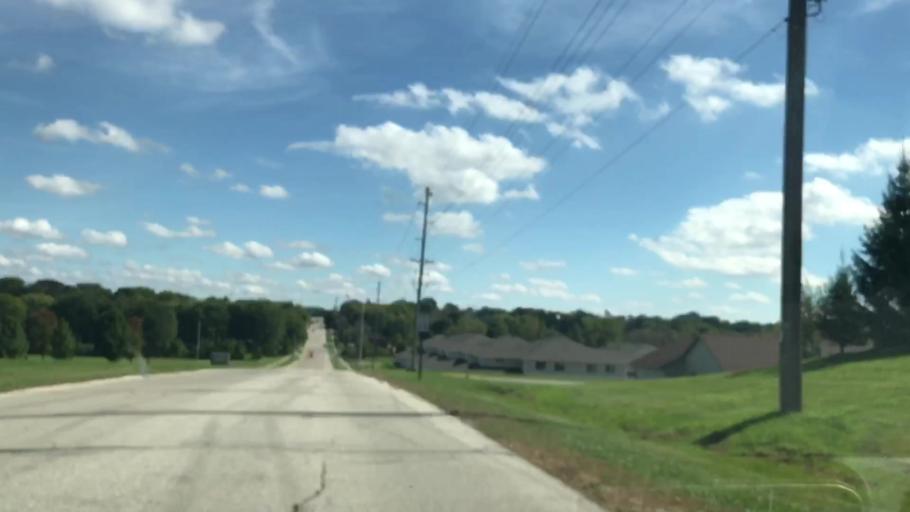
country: US
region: Wisconsin
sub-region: Dodge County
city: Mayville
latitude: 43.5014
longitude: -88.5650
